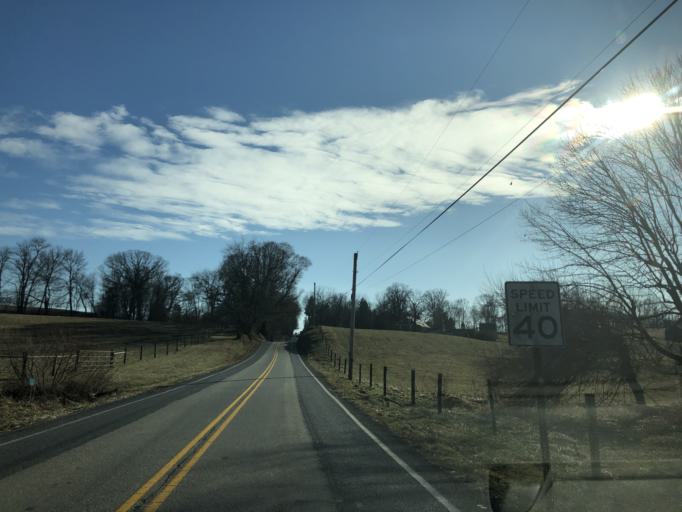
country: US
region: Pennsylvania
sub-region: Chester County
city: Upland
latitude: 39.8741
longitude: -75.7733
